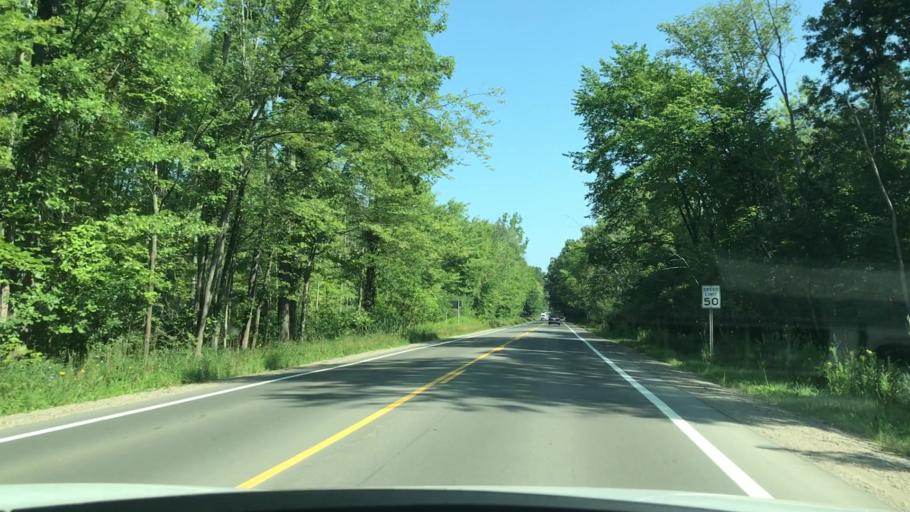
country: US
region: Michigan
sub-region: Oakland County
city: Oxford
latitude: 42.7870
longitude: -83.3327
